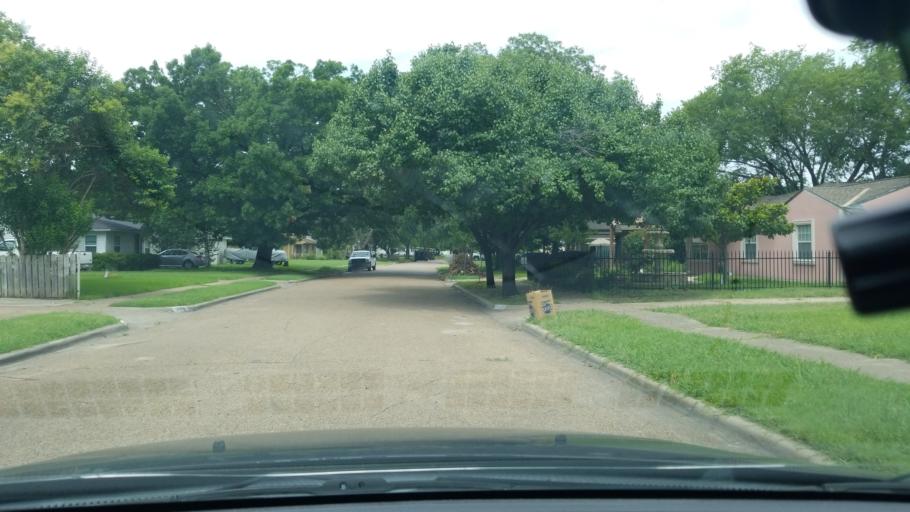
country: US
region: Texas
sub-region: Dallas County
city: Mesquite
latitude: 32.8243
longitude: -96.6736
